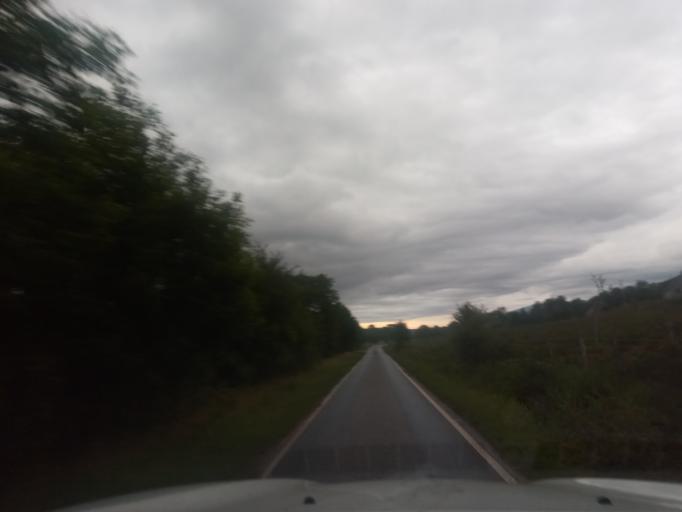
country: GB
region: Scotland
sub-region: Highland
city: Fort William
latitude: 56.8470
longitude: -5.3057
